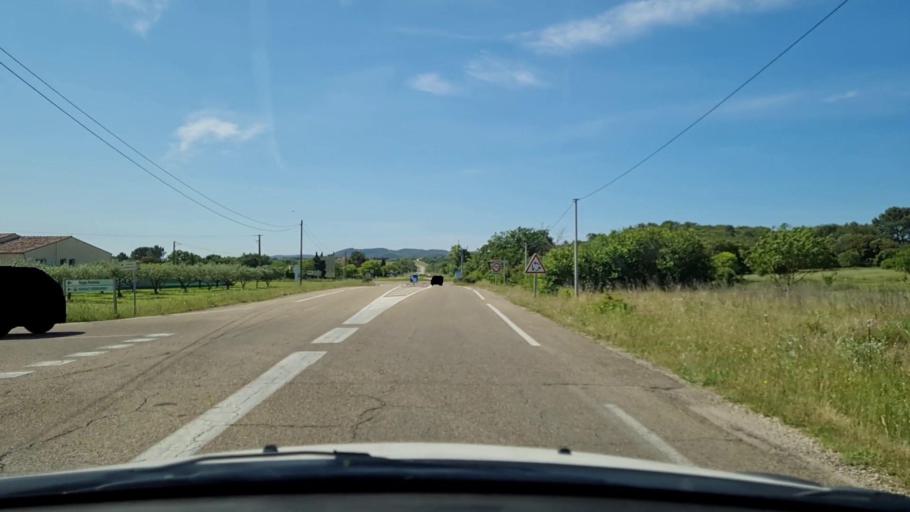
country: FR
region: Languedoc-Roussillon
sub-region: Departement du Gard
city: Vezenobres
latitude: 44.0444
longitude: 4.1455
